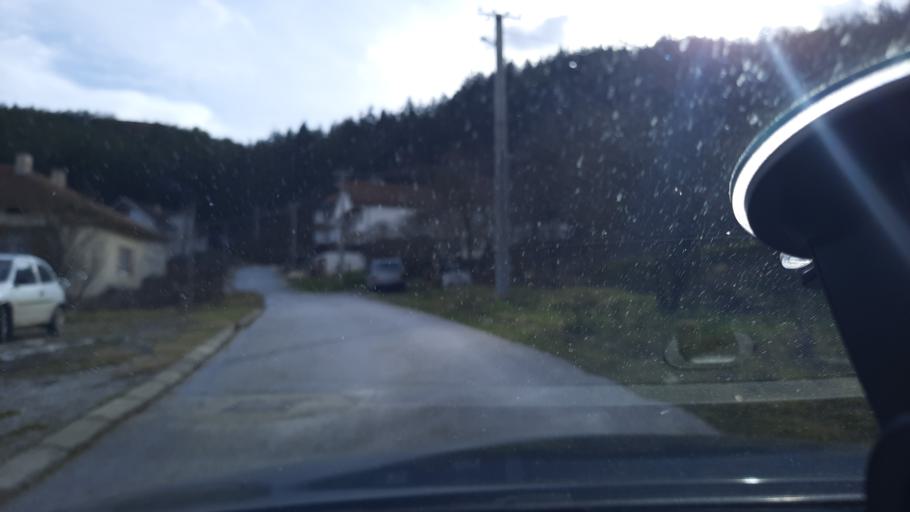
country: MK
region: Makedonski Brod
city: Makedonski Brod
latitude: 41.5060
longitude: 21.2174
